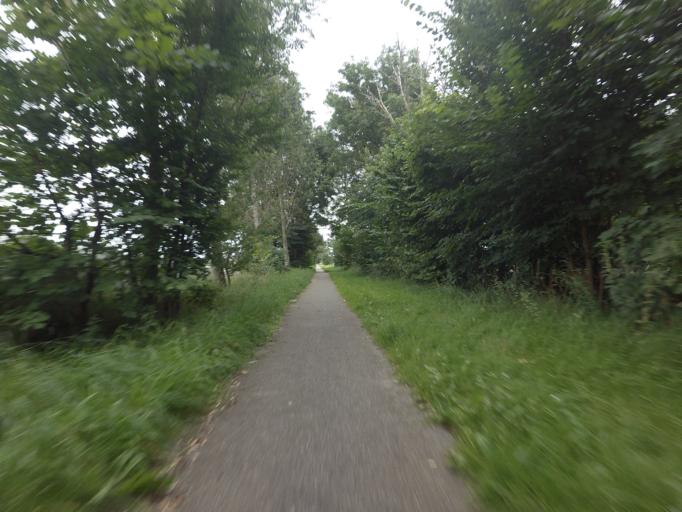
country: DK
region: Central Jutland
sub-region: Horsens Kommune
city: Braedstrup
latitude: 56.0224
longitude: 9.5711
